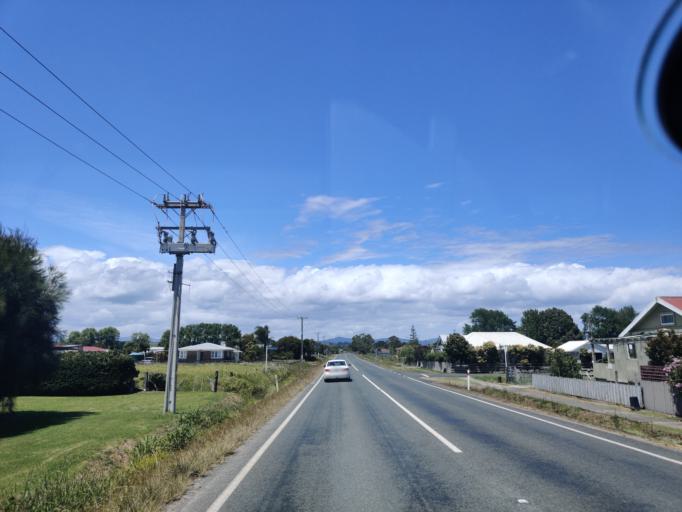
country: NZ
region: Northland
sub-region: Far North District
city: Kaitaia
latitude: -35.0396
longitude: 173.2553
